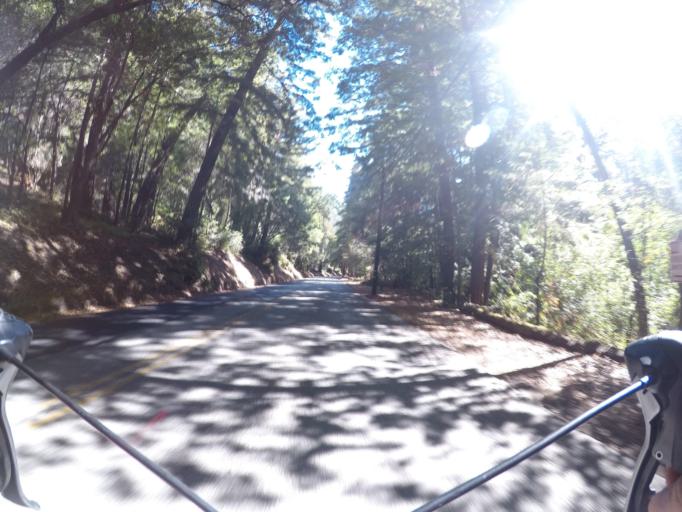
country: US
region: California
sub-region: San Mateo County
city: Portola Valley
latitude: 37.2764
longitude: -122.2894
